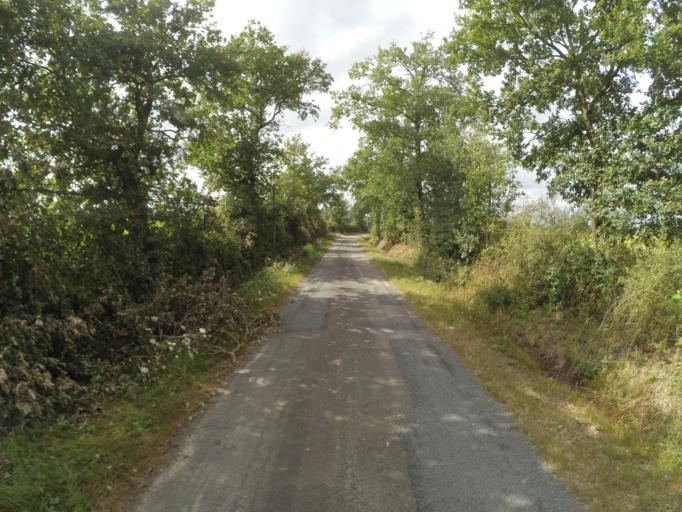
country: FR
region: Pays de la Loire
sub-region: Departement de la Vendee
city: Saint-Philbert-de-Bouaine
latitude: 46.9942
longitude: -1.4847
